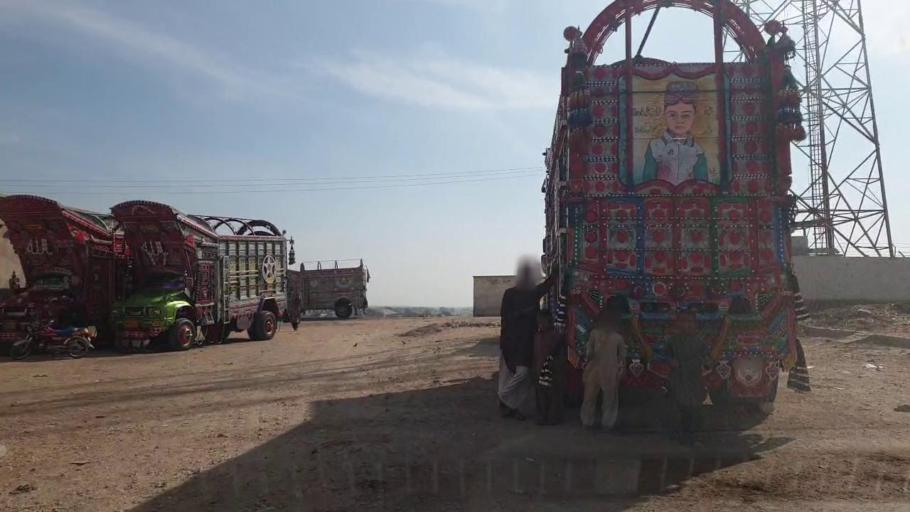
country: PK
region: Sindh
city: Hala
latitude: 25.7615
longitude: 68.2912
